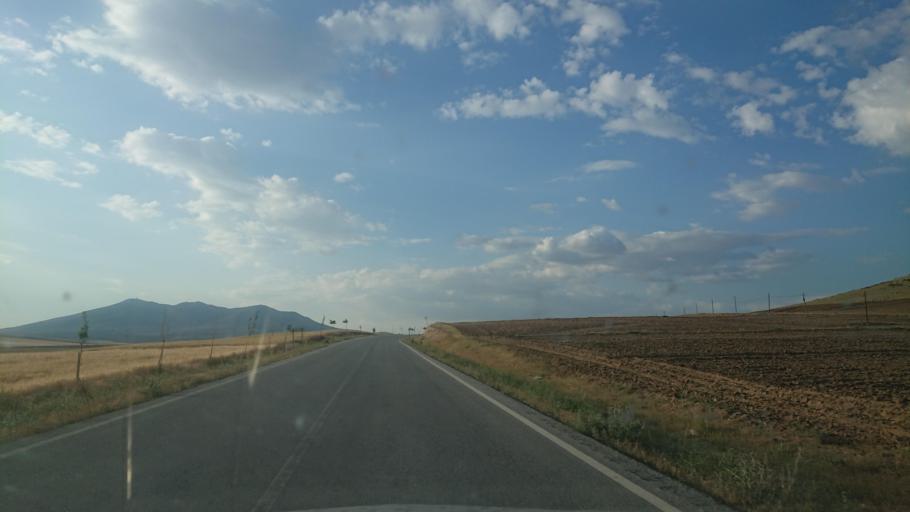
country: TR
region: Aksaray
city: Balci
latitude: 38.5485
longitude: 34.1032
